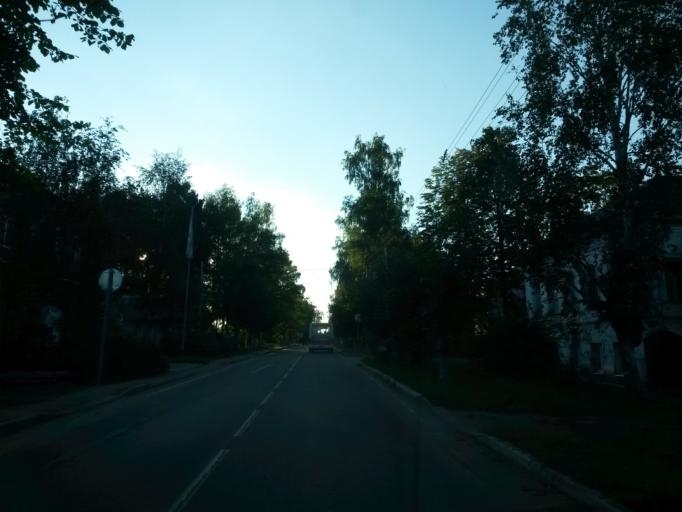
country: RU
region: Jaroslavl
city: Tutayev
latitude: 57.8701
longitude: 39.5324
